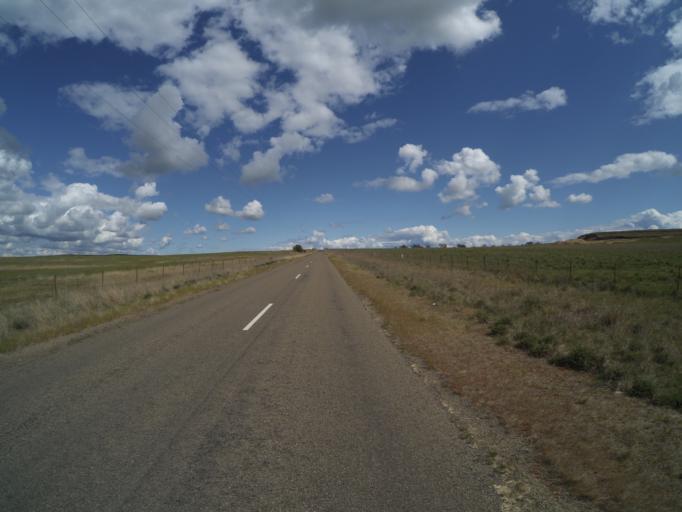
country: AU
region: New South Wales
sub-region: Yass Valley
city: Yass
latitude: -34.8879
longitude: 148.8945
